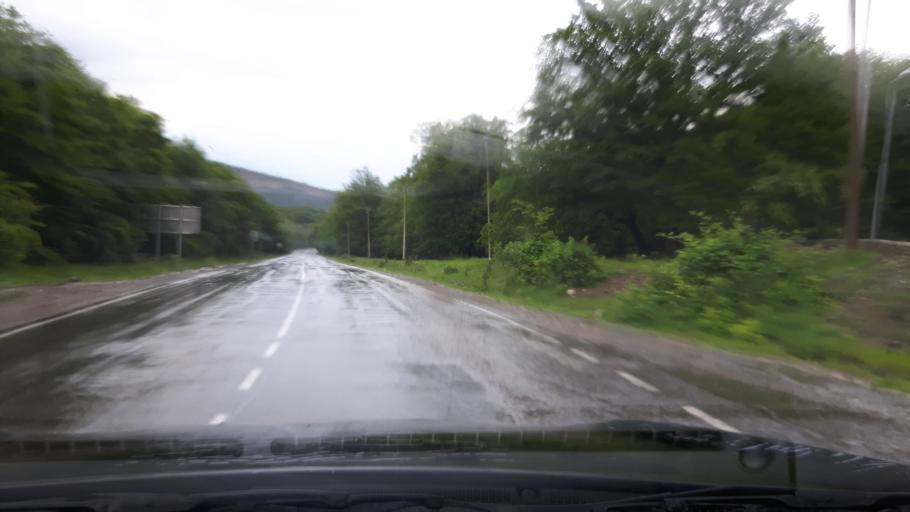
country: GE
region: Kakheti
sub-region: Telavi
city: Telavi
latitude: 41.9150
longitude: 45.3877
